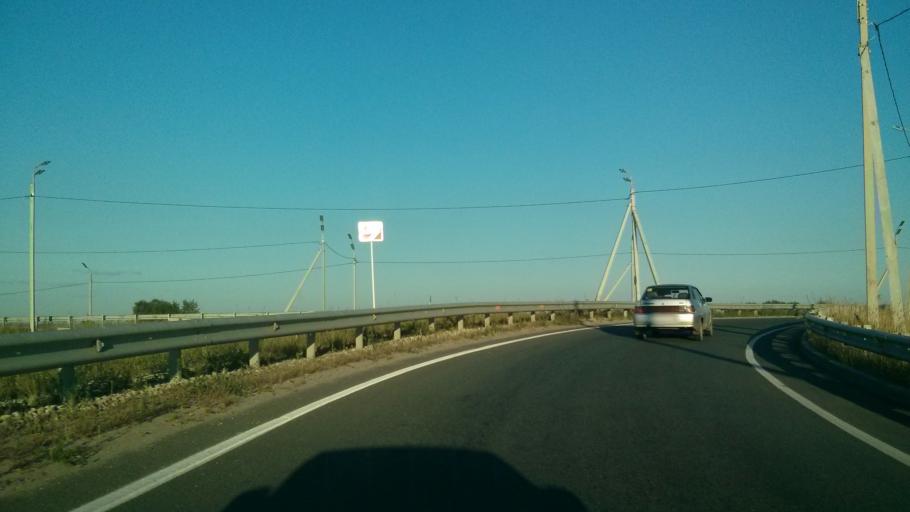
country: RU
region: Vladimir
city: Murom
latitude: 55.6199
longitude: 42.0236
